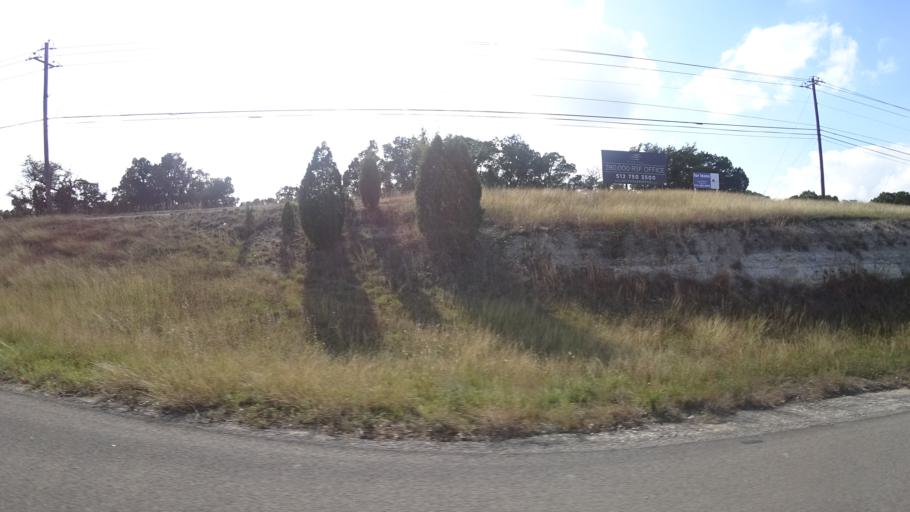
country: US
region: Texas
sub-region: Travis County
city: Lost Creek
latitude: 30.3167
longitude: -97.8596
